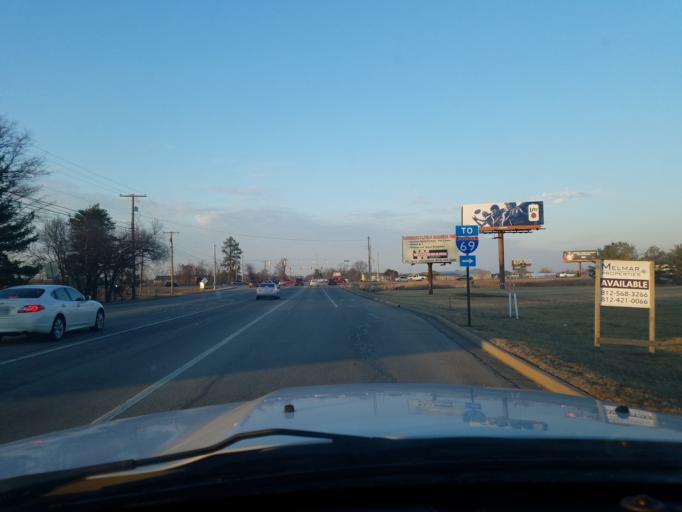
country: US
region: Indiana
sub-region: Vanderburgh County
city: Melody Hill
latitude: 38.0112
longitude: -87.4735
